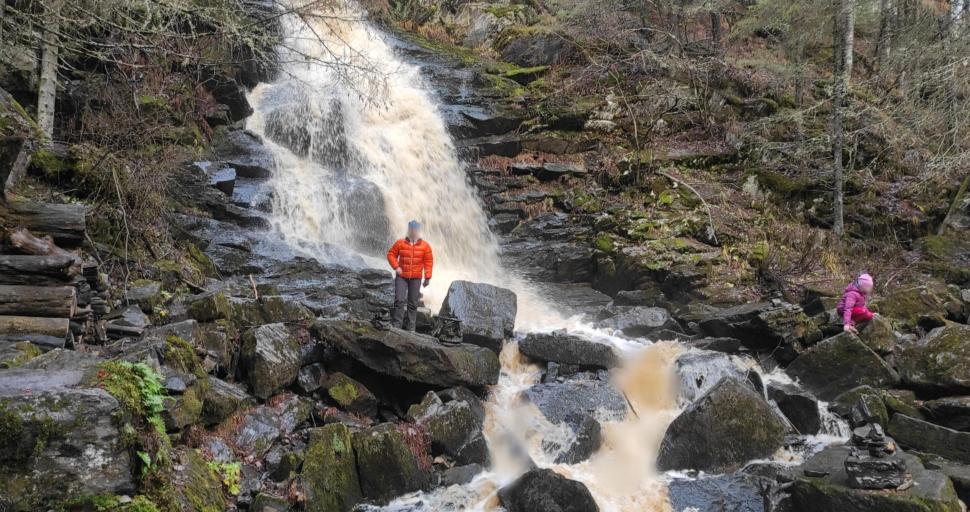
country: RU
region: Republic of Karelia
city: Pitkyaranta
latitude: 61.7539
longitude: 31.4116
